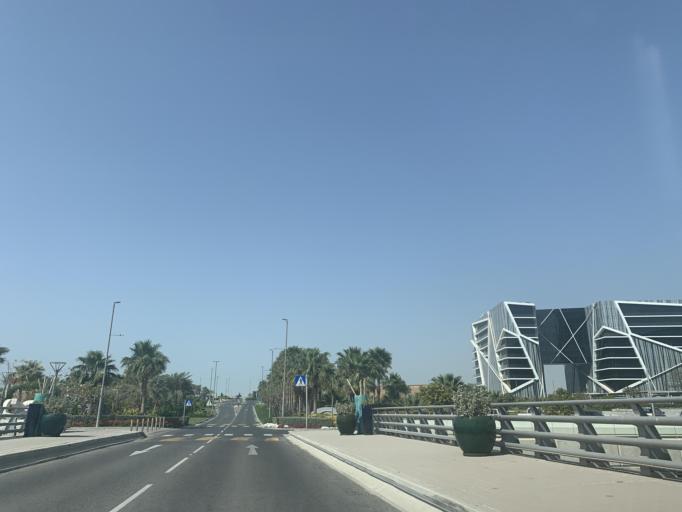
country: BH
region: Muharraq
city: Al Muharraq
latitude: 26.2494
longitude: 50.5818
